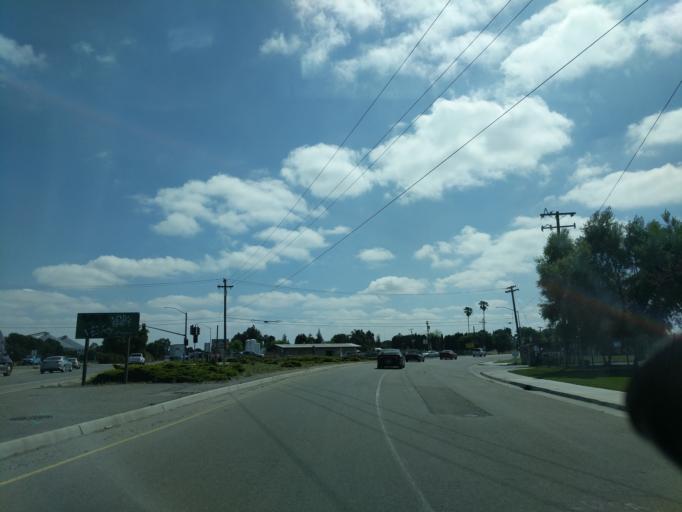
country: US
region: California
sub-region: San Joaquin County
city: Kennedy
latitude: 37.9445
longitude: -121.2566
